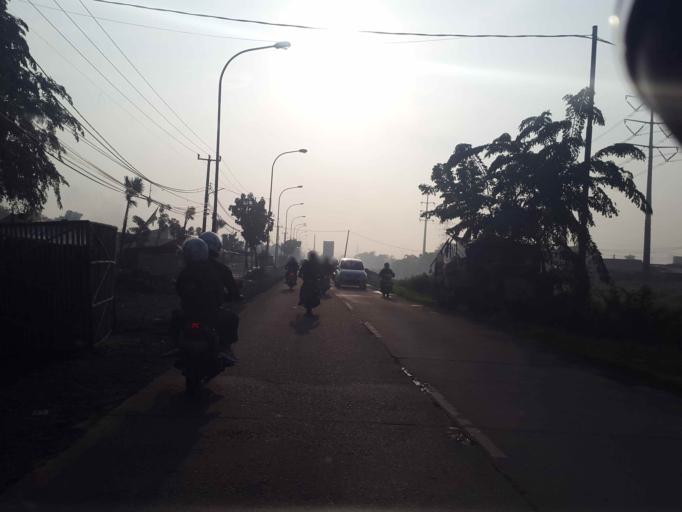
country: ID
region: West Java
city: Bekasi
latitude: -6.2655
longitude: 107.0308
